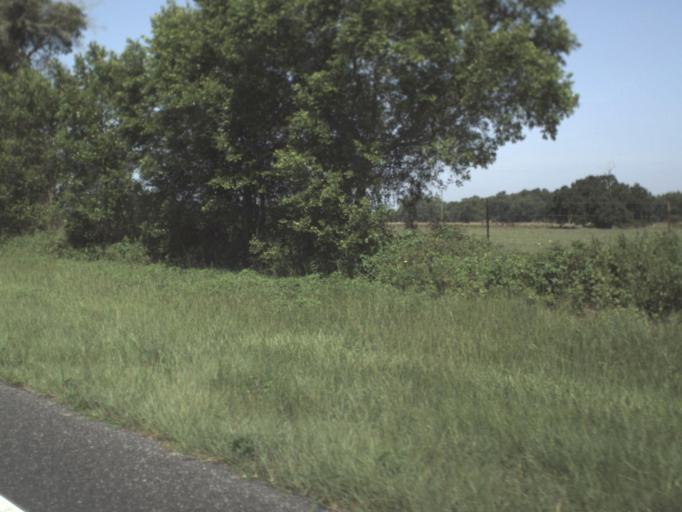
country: US
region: Florida
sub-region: Levy County
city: Chiefland
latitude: 29.5009
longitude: -82.8366
